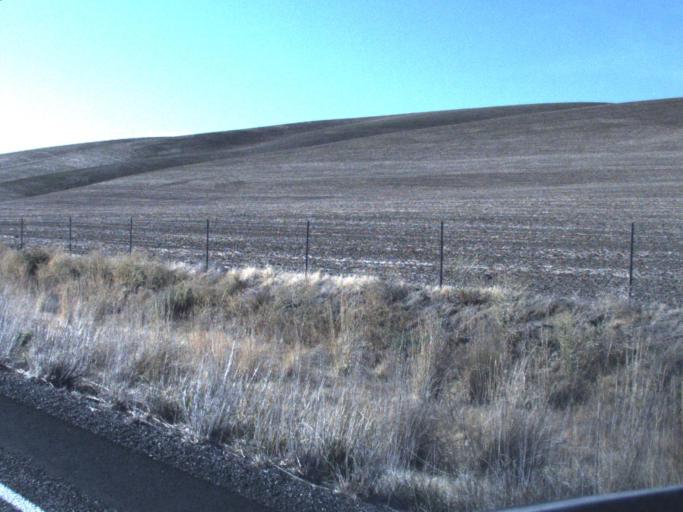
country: US
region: Washington
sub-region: Walla Walla County
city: Walla Walla
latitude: 46.2993
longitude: -118.4182
